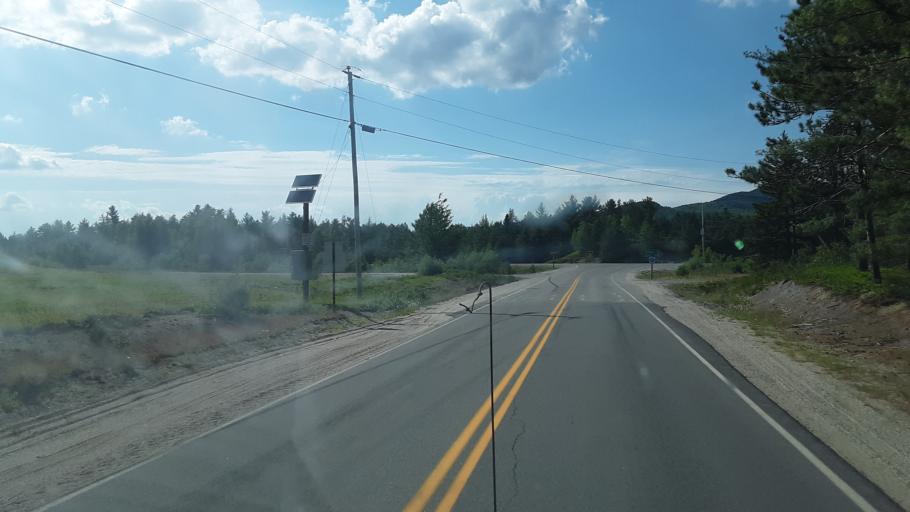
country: US
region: Maine
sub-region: Washington County
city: Cherryfield
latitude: 44.8287
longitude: -68.0830
